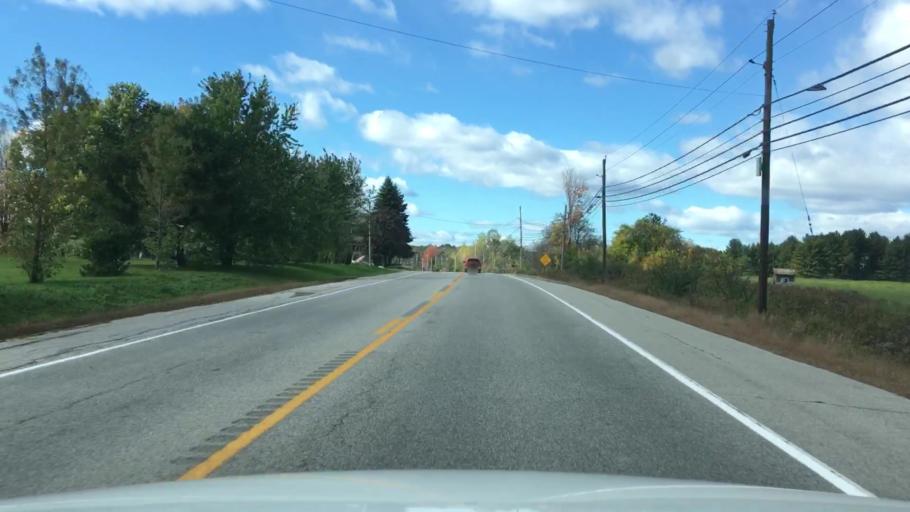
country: US
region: Maine
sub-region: York County
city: West Kennebunk
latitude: 43.4770
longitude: -70.5587
